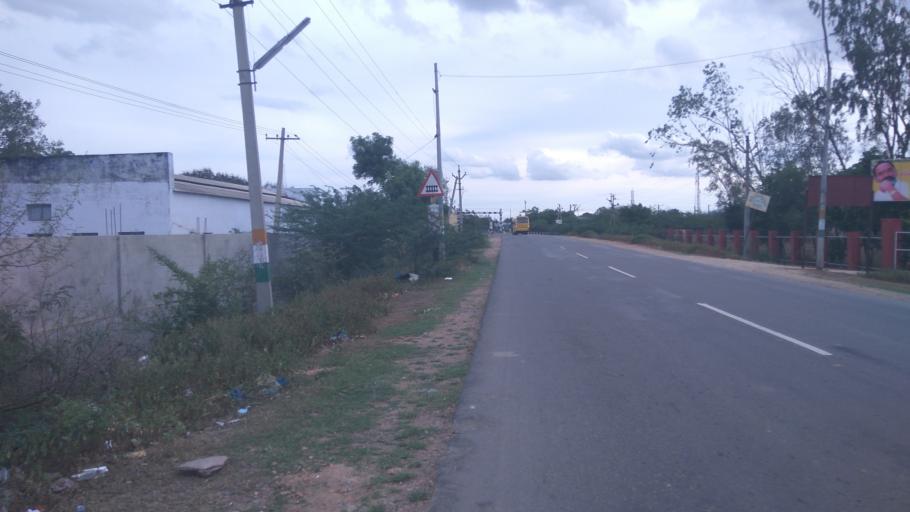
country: IN
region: Andhra Pradesh
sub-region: Prakasam
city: Cumbum
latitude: 15.5949
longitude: 79.1168
